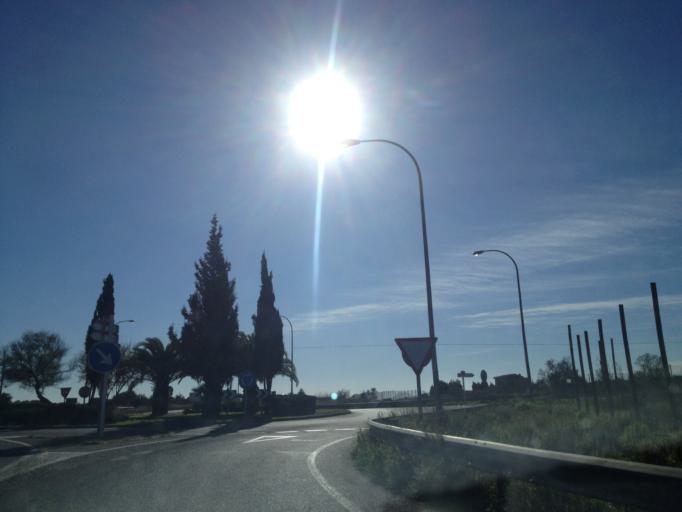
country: ES
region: Balearic Islands
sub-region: Illes Balears
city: Petra
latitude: 39.6174
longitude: 3.1214
